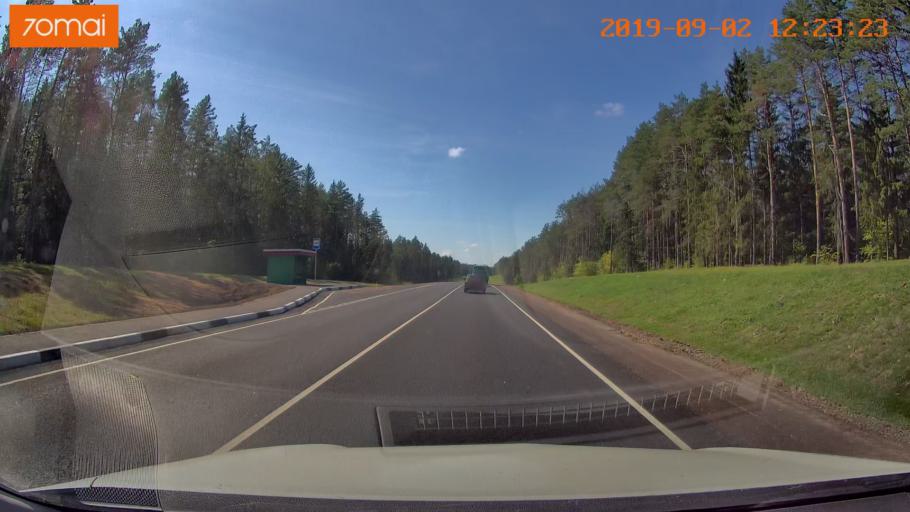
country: RU
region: Smolensk
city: Shumyachi
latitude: 53.8748
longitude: 32.6209
